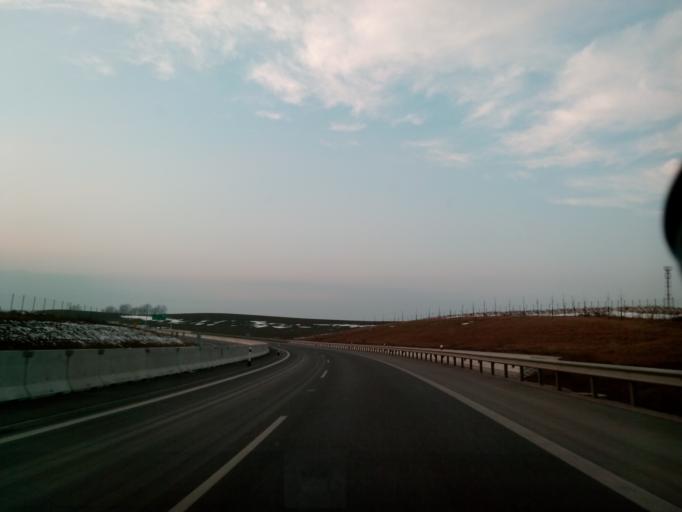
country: HU
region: Borsod-Abauj-Zemplen
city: Gonc
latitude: 48.5399
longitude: 21.2463
